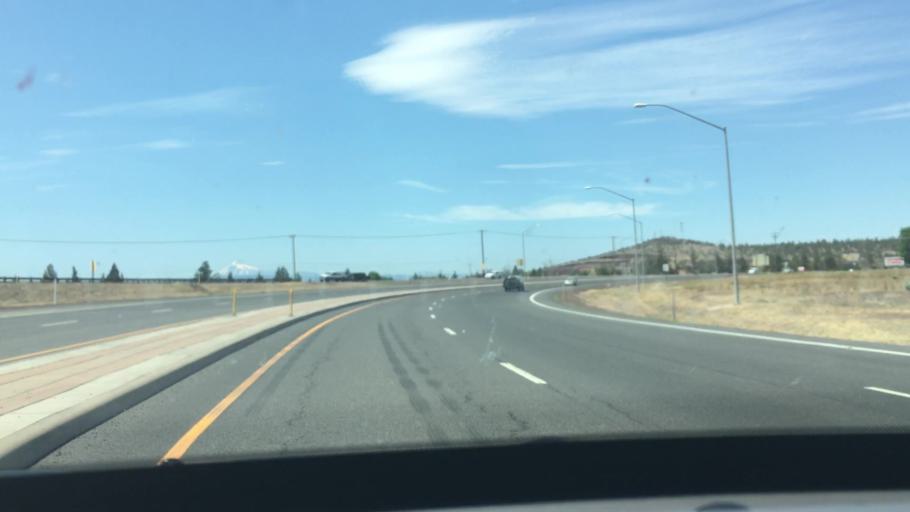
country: US
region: Oregon
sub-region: Deschutes County
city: Redmond
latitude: 44.3014
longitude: -121.1720
